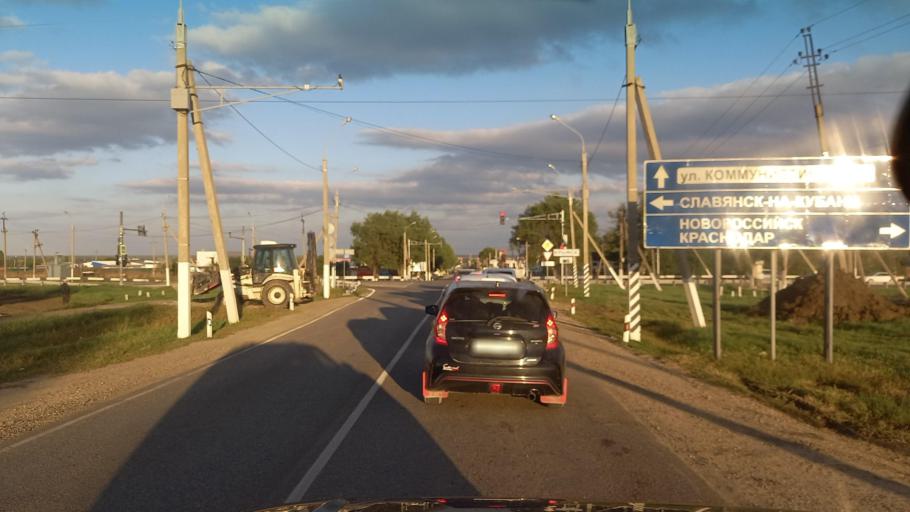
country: RU
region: Krasnodarskiy
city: Krymsk
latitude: 44.9378
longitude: 37.9608
